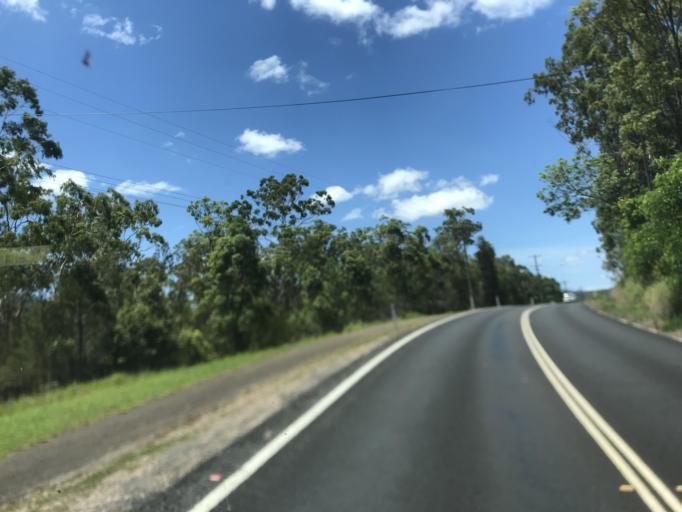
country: AU
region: Queensland
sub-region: Tablelands
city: Atherton
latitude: -17.3934
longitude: 145.3876
